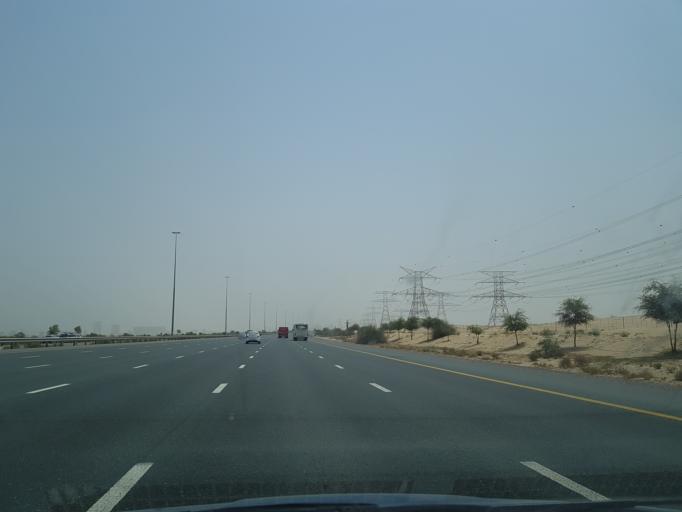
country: AE
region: Dubai
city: Dubai
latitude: 25.0638
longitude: 55.3328
